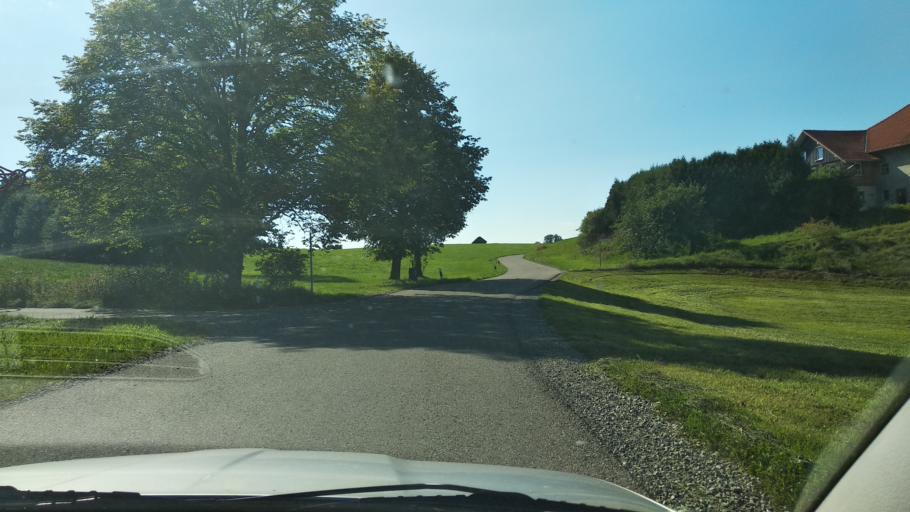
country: DE
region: Bavaria
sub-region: Swabia
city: Legau
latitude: 47.8274
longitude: 10.0948
